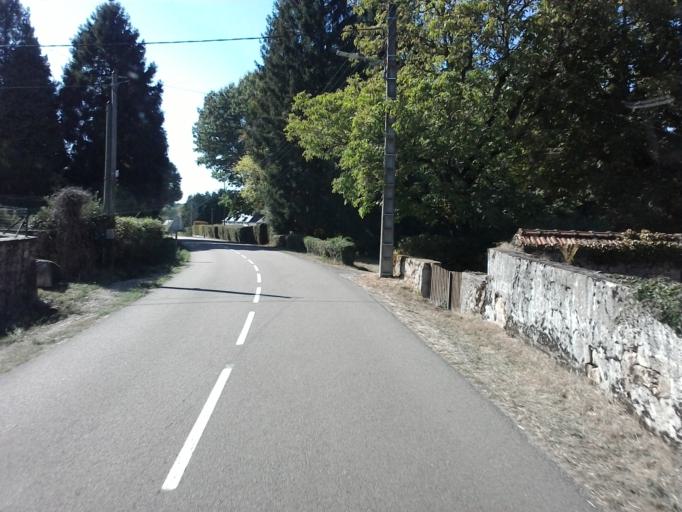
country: FR
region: Bourgogne
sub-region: Departement de la Nievre
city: Lormes
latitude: 47.2843
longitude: 4.0087
